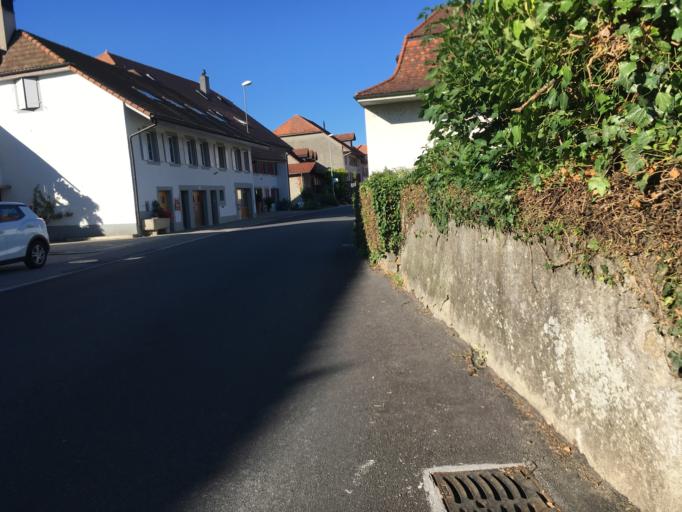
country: CH
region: Fribourg
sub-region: See District
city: Bas-Vully
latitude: 46.9537
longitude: 7.0987
